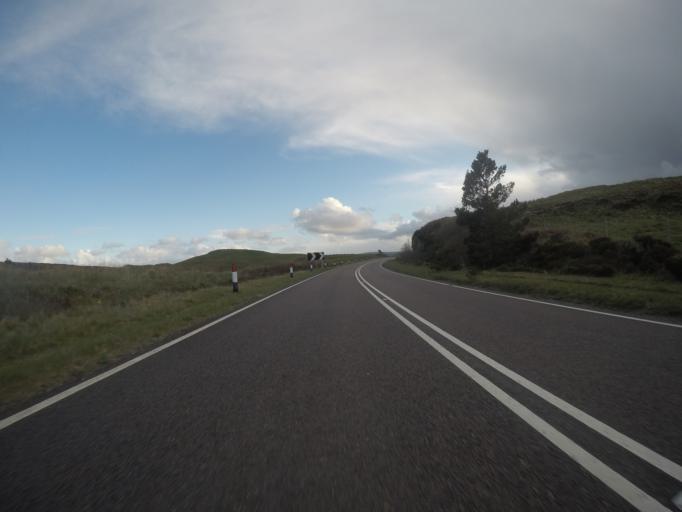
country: GB
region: Scotland
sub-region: Highland
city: Portree
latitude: 57.5480
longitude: -6.3635
